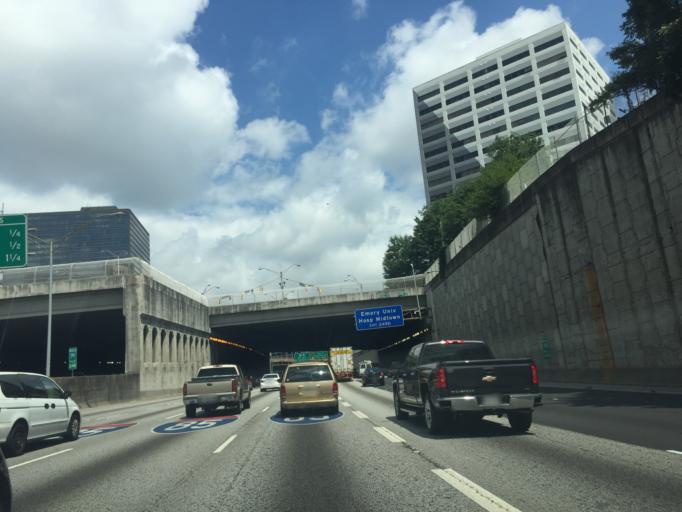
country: US
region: Georgia
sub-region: Fulton County
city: Atlanta
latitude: 33.7635
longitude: -84.3832
